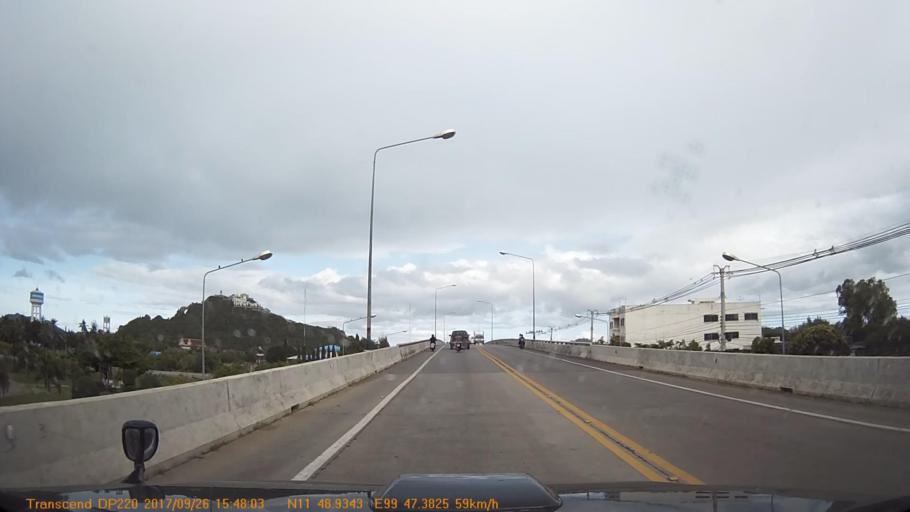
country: TH
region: Prachuap Khiri Khan
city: Prachuap Khiri Khan
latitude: 11.8155
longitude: 99.7899
